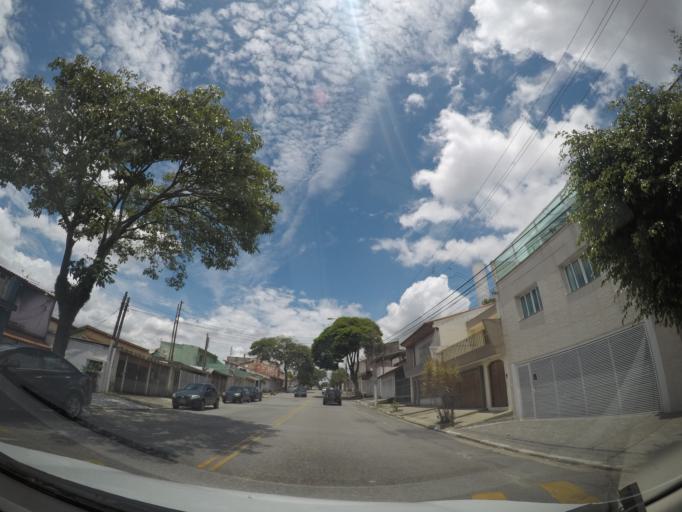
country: BR
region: Sao Paulo
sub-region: Guarulhos
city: Guarulhos
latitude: -23.4505
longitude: -46.5287
